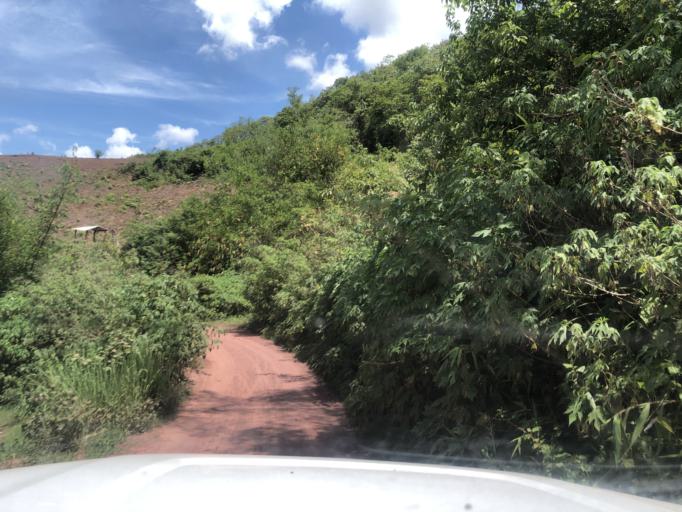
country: CN
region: Yunnan
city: Menglie
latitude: 22.2409
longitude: 101.6156
